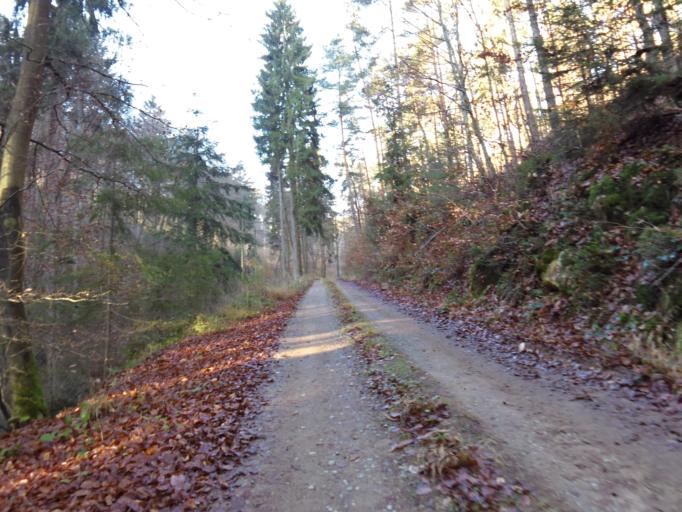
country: DE
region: Rheinland-Pfalz
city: Altleiningen
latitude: 49.4776
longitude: 8.1046
